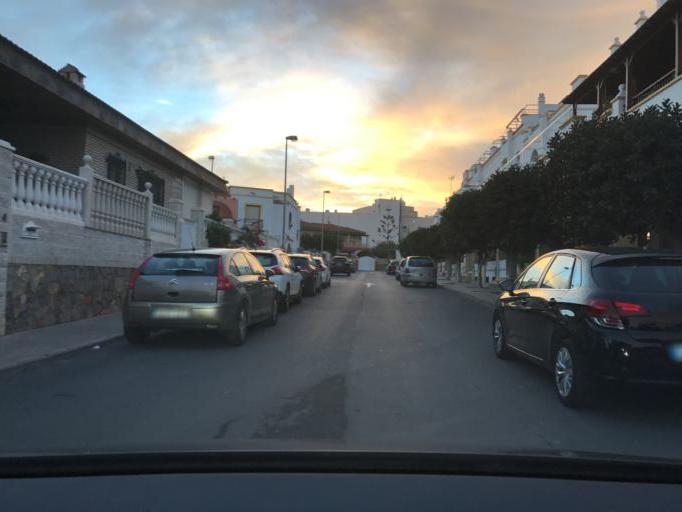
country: ES
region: Andalusia
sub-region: Provincia de Almeria
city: Aguadulce
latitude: 36.8118
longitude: -2.5797
